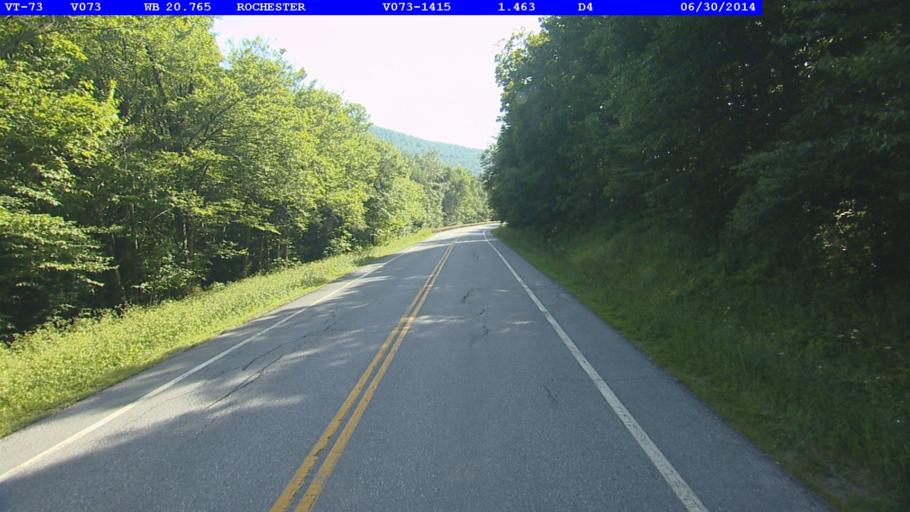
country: US
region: Vermont
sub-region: Rutland County
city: Brandon
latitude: 43.8421
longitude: -72.9356
